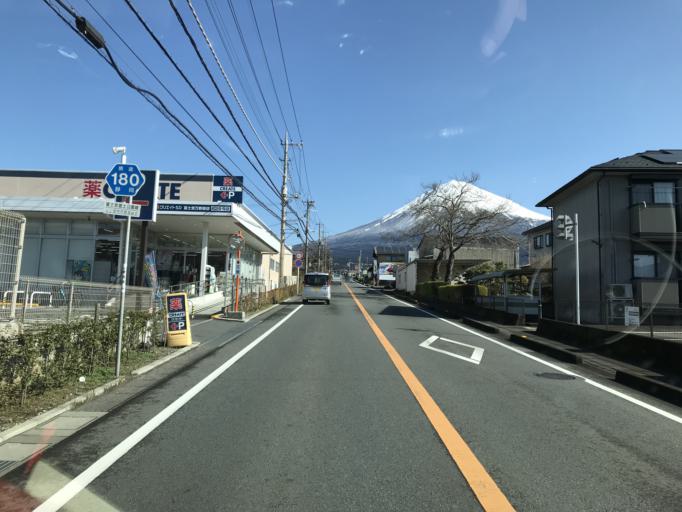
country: JP
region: Shizuoka
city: Fujinomiya
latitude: 35.2504
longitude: 138.6276
